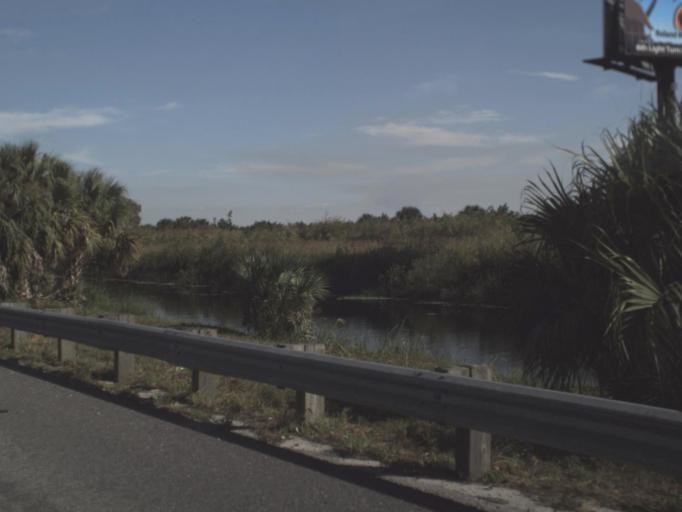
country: US
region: Florida
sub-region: Glades County
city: Moore Haven
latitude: 26.7537
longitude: -81.0462
